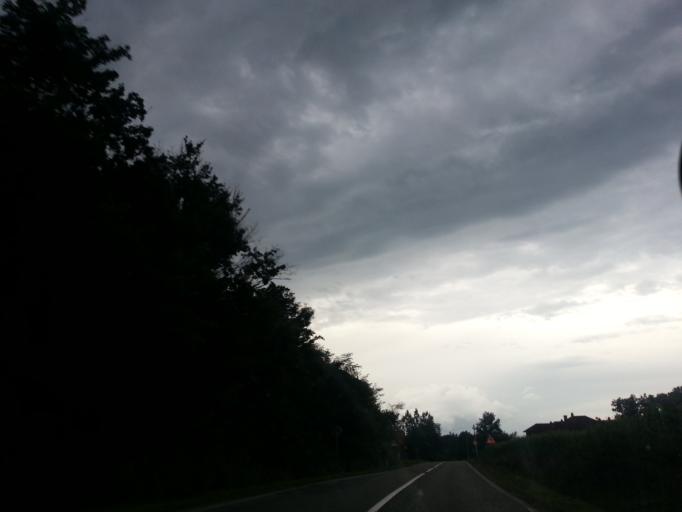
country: BA
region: Republika Srpska
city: Velika Obarska
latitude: 44.7763
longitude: 19.1108
